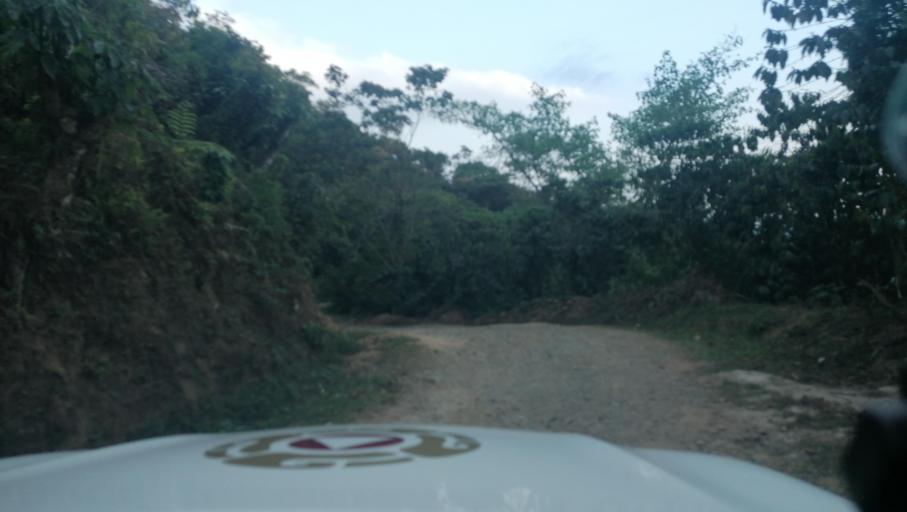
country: MX
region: Chiapas
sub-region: Cacahoatan
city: Benito Juarez
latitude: 15.0985
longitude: -92.2200
